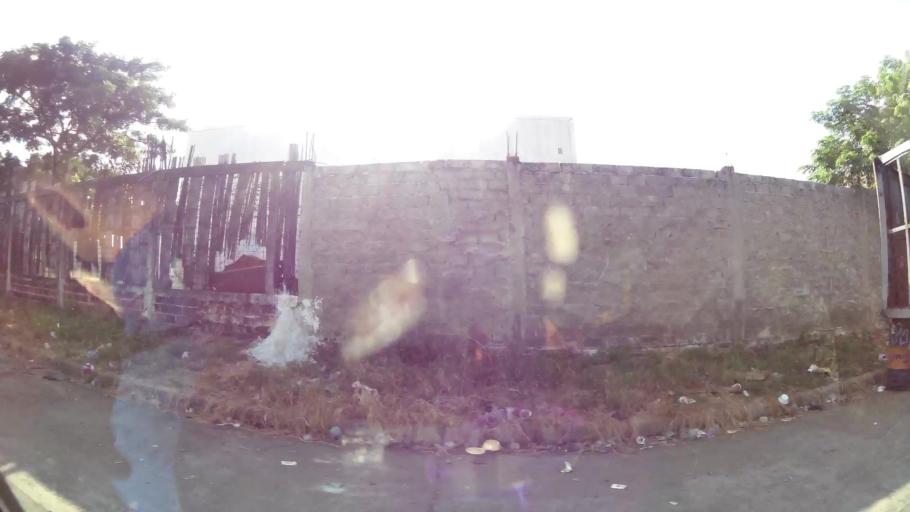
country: EC
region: Guayas
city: Eloy Alfaro
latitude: -2.0708
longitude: -79.9279
